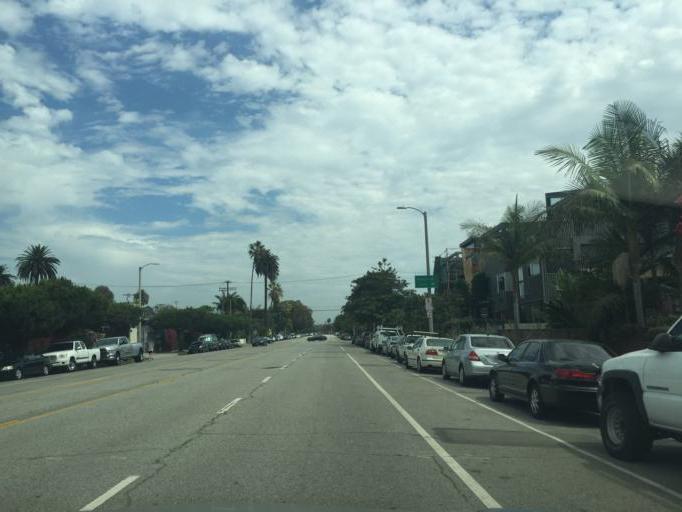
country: US
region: California
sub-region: Los Angeles County
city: Marina del Rey
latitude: 33.9881
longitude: -118.4703
